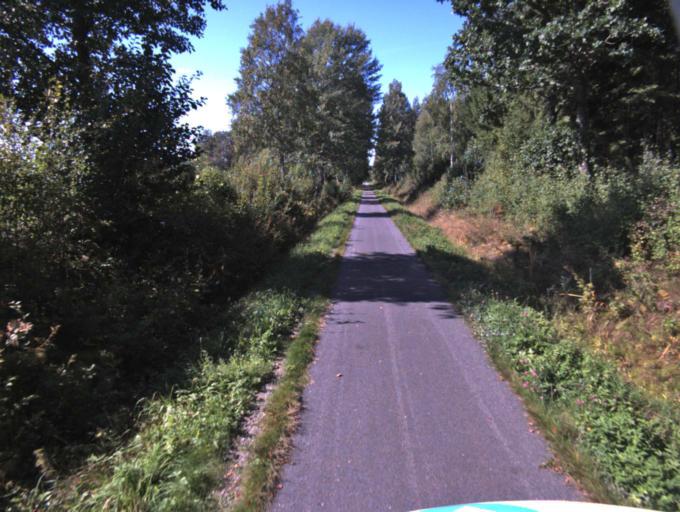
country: SE
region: Vaestra Goetaland
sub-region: Ulricehamns Kommun
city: Ulricehamn
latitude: 57.7999
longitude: 13.3824
